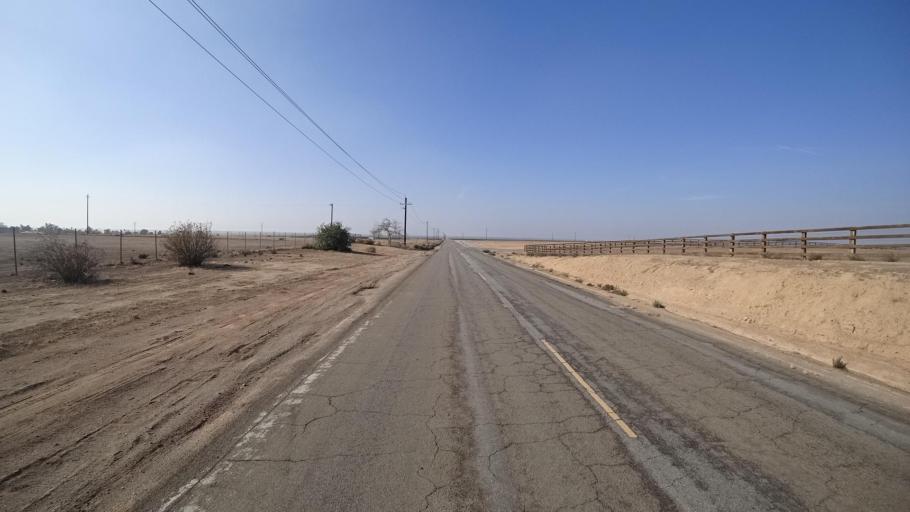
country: US
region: California
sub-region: Kern County
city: Oildale
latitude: 35.5299
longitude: -119.1033
